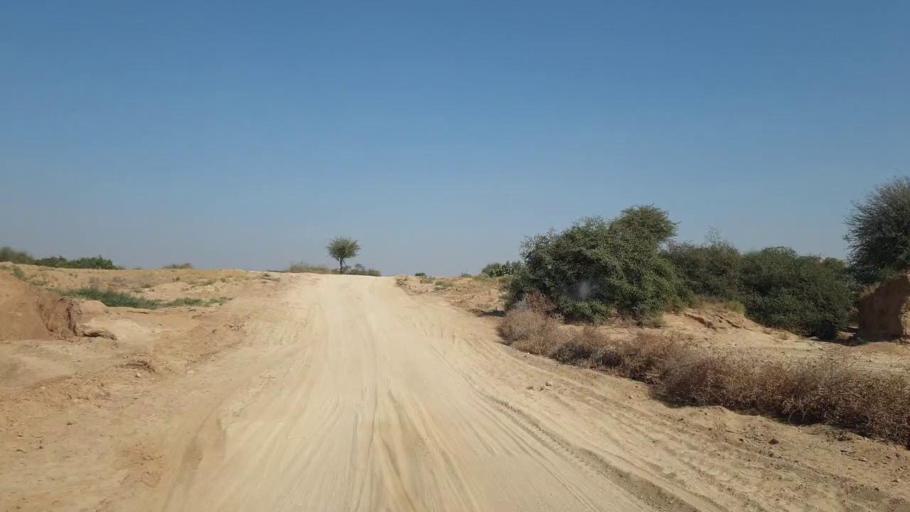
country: PK
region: Sindh
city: Jamshoro
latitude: 25.2816
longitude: 67.8088
